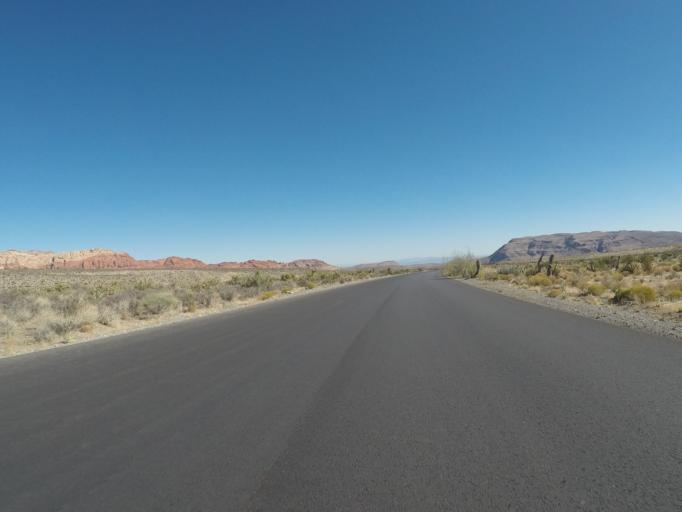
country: US
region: Nevada
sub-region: Clark County
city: Summerlin South
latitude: 36.1420
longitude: -115.4711
